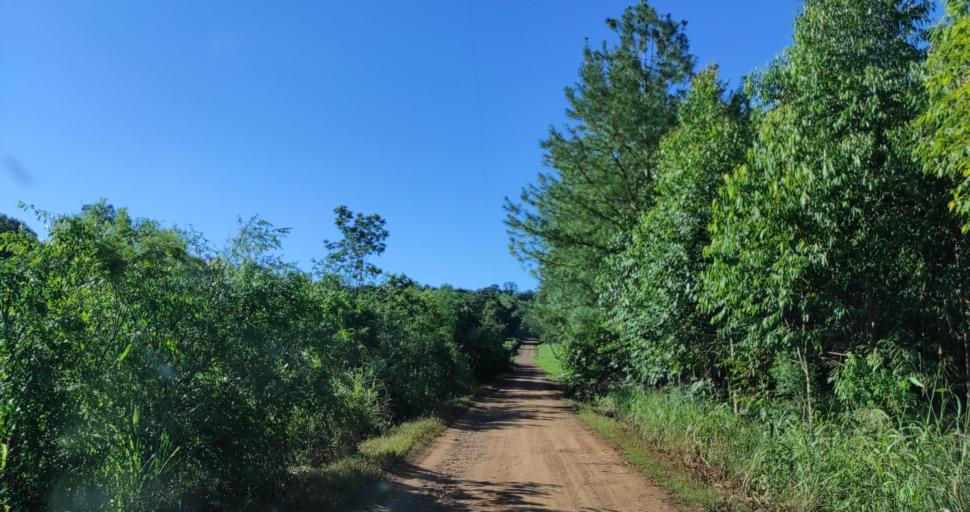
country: AR
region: Misiones
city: Capiovi
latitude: -26.9116
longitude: -54.9994
